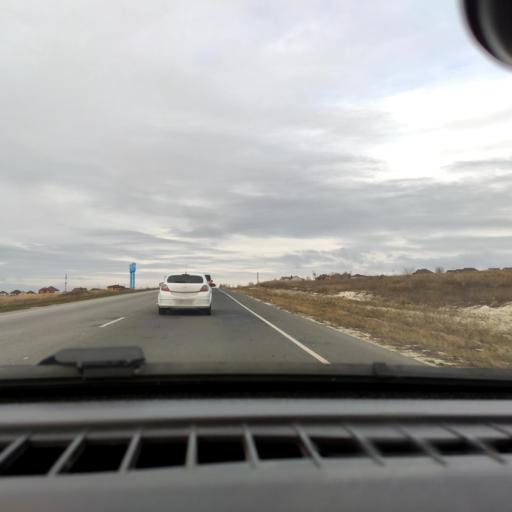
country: RU
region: Belgorod
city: Alekseyevka
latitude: 50.6453
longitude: 38.6386
